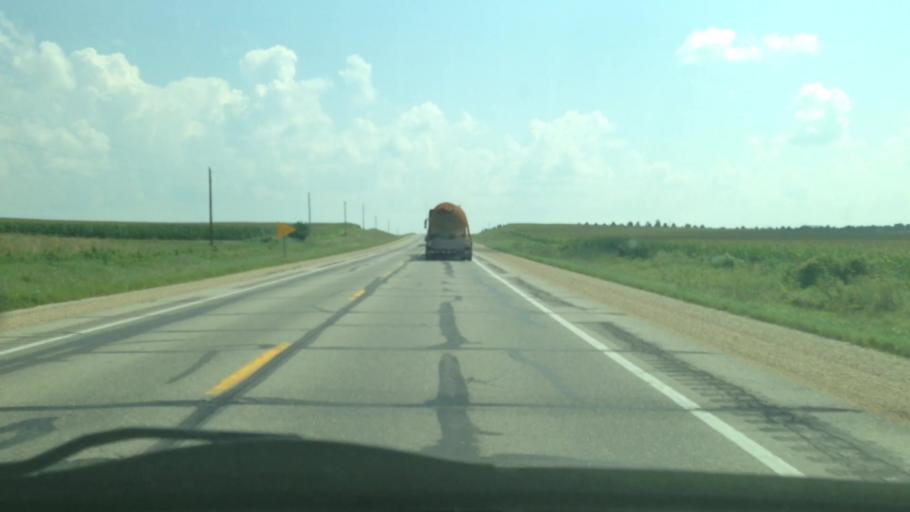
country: US
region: Iowa
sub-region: Chickasaw County
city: New Hampton
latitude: 43.1965
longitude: -92.2983
